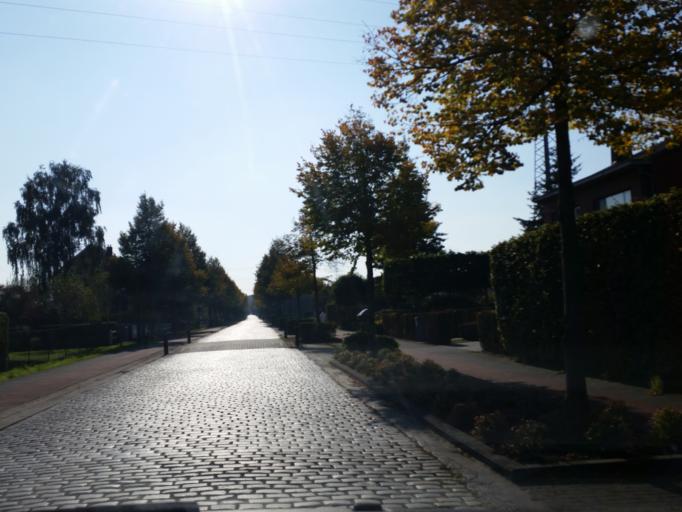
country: BE
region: Flanders
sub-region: Provincie Antwerpen
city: Kontich
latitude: 51.1193
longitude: 4.4437
